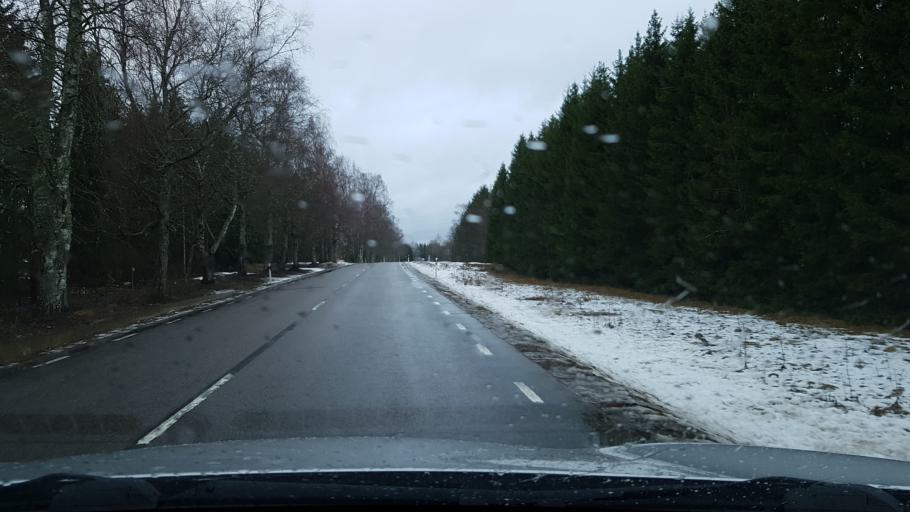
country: LV
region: Apes Novads
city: Ape
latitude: 57.6064
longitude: 26.6108
